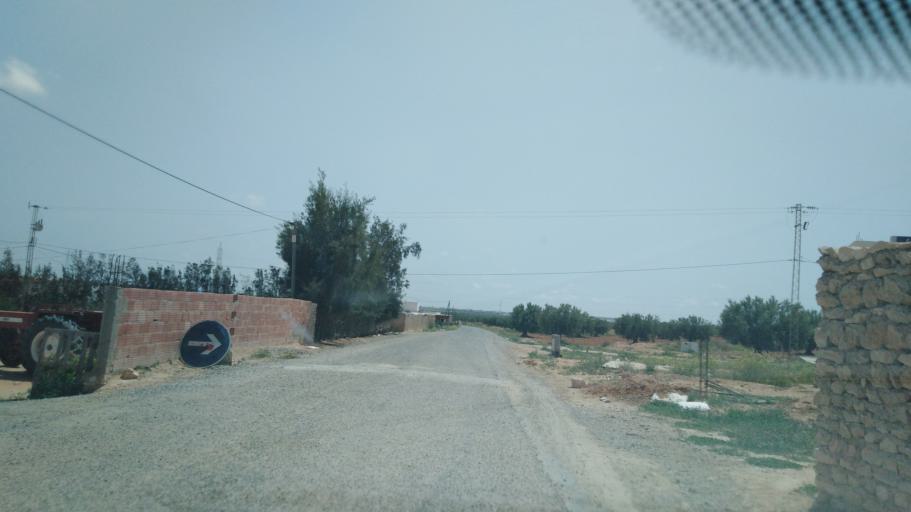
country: TN
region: Safaqis
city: Sfax
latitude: 34.7492
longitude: 10.5698
